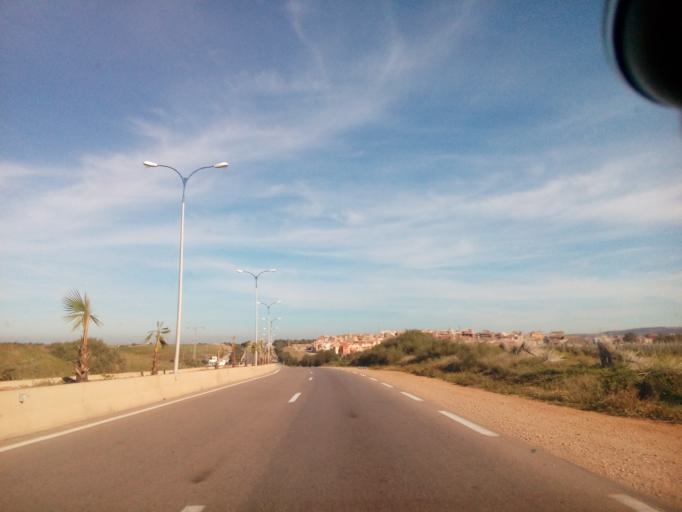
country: DZ
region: Mostaganem
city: Mostaganem
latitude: 35.8259
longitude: -0.0123
